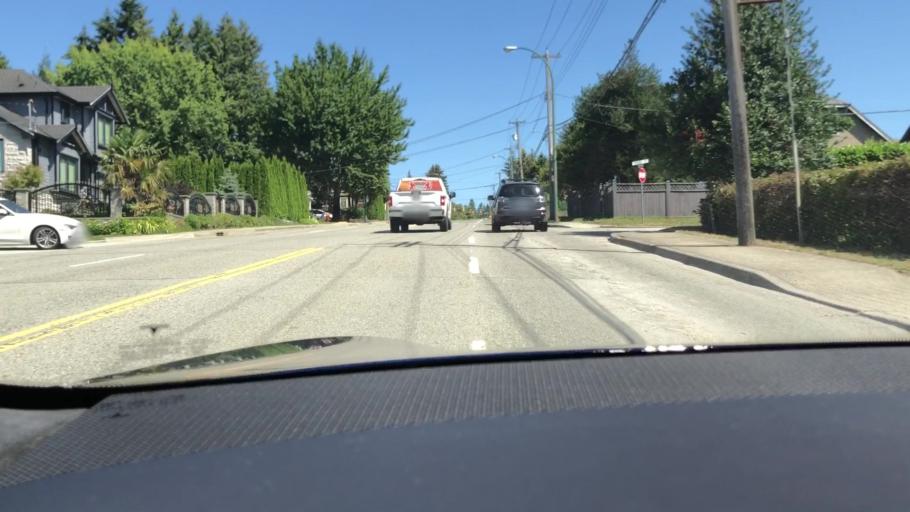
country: CA
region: British Columbia
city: Port Moody
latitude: 49.2425
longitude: -122.8730
